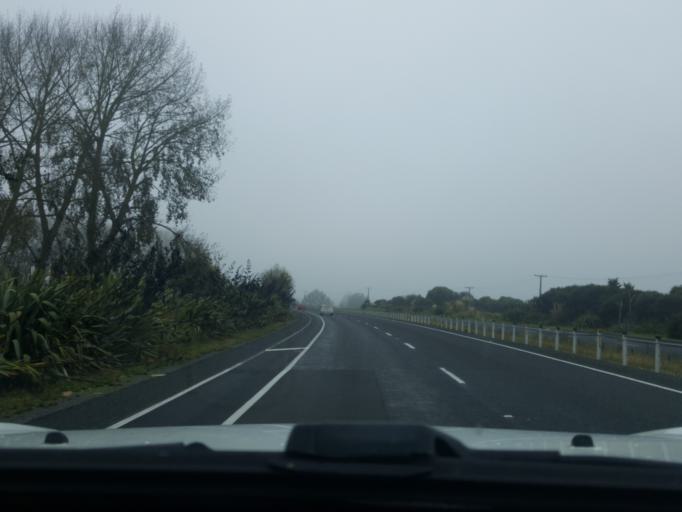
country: NZ
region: Waikato
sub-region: Waikato District
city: Te Kauwhata
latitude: -37.4457
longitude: 175.1517
